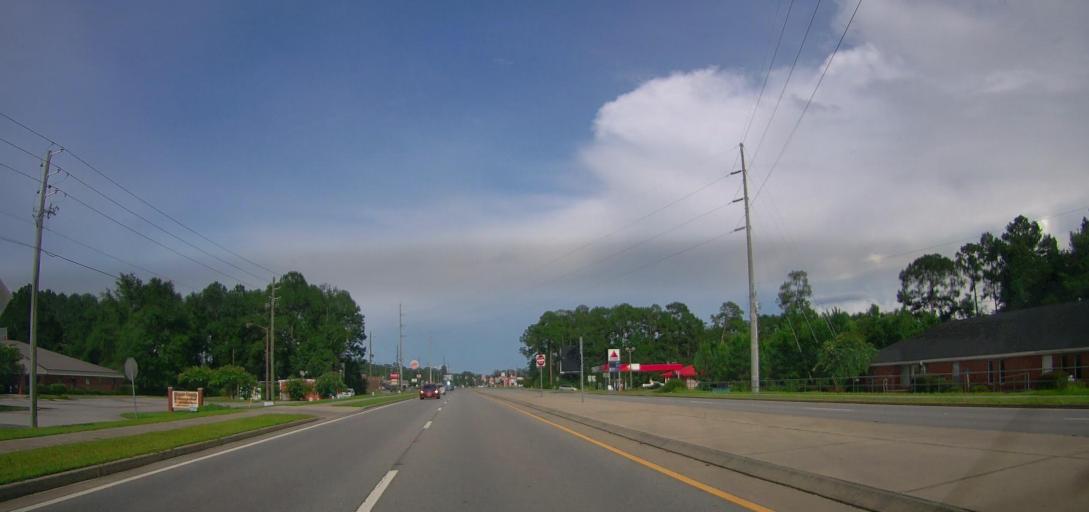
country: US
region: Georgia
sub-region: Wayne County
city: Jesup
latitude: 31.6049
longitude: -81.9111
